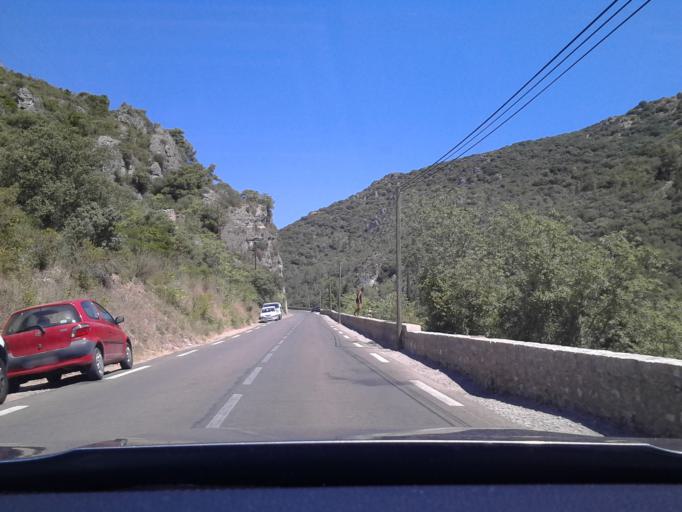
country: FR
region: Languedoc-Roussillon
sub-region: Departement de l'Herault
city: Saint-Jean-de-Fos
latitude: 43.7192
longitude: 3.5535
